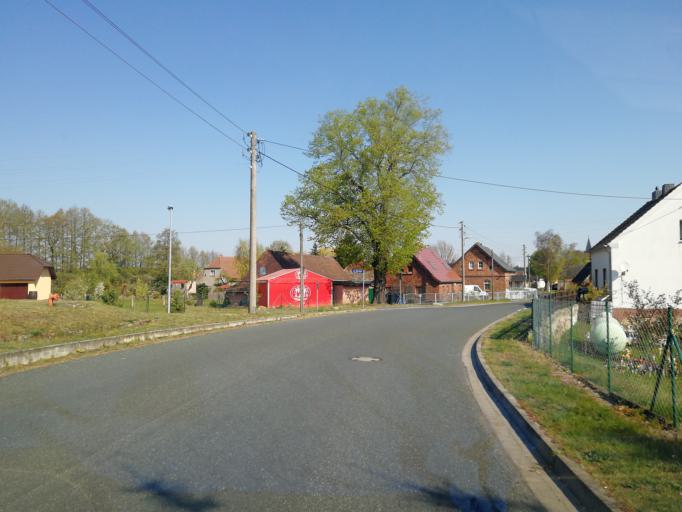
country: DE
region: Brandenburg
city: Bronkow
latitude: 51.6995
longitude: 13.8744
